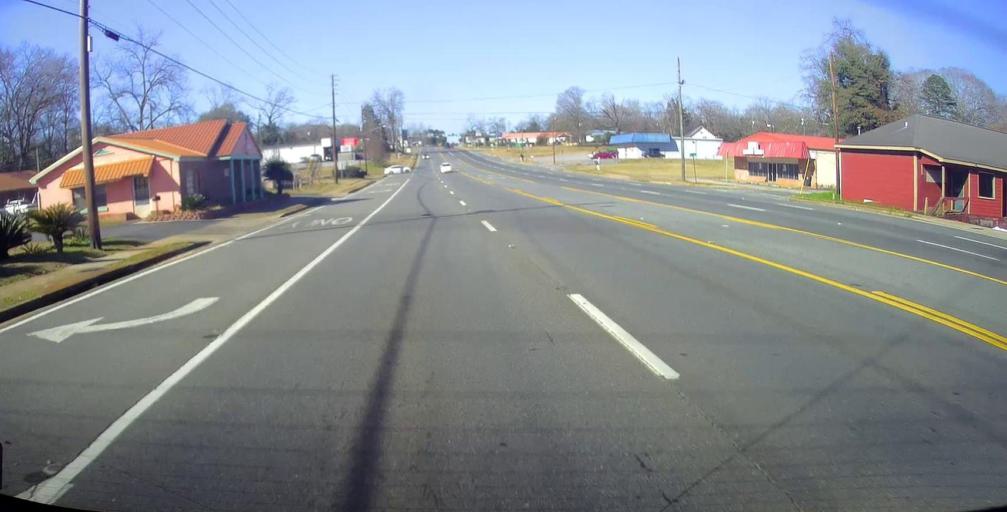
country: US
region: Georgia
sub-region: Sumter County
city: Americus
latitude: 32.0824
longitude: -84.2393
